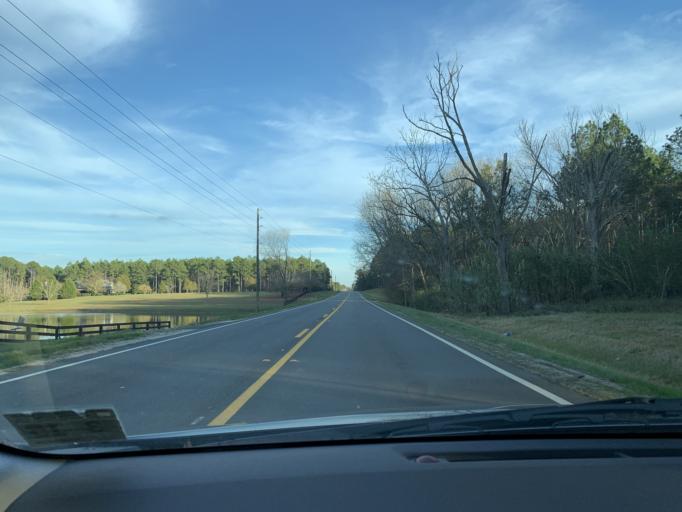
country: US
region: Georgia
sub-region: Irwin County
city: Ocilla
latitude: 31.5834
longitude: -83.0711
